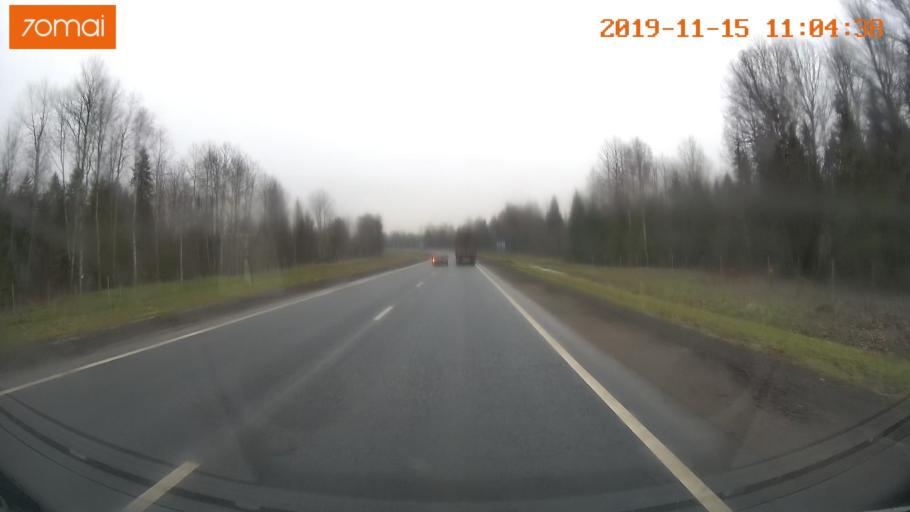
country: RU
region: Vologda
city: Chebsara
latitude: 59.1194
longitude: 38.9871
